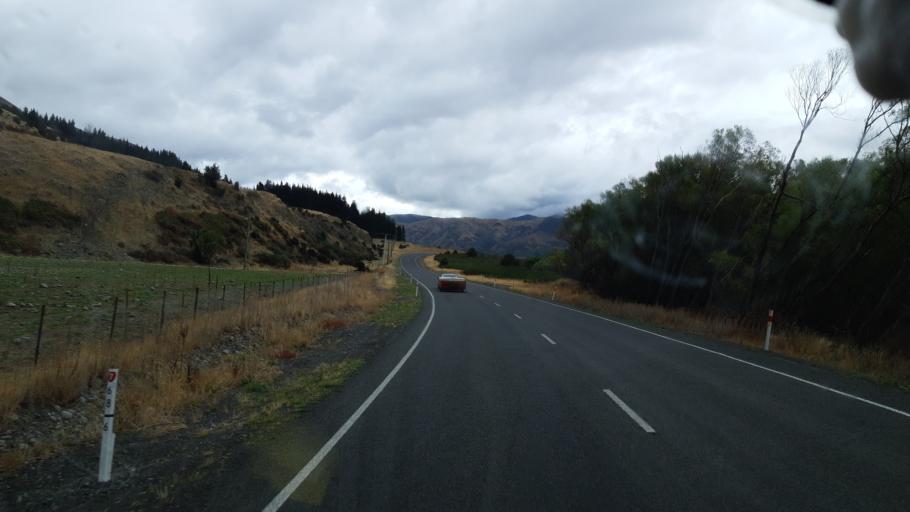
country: NZ
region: Canterbury
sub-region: Hurunui District
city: Amberley
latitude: -42.5732
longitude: 172.7173
